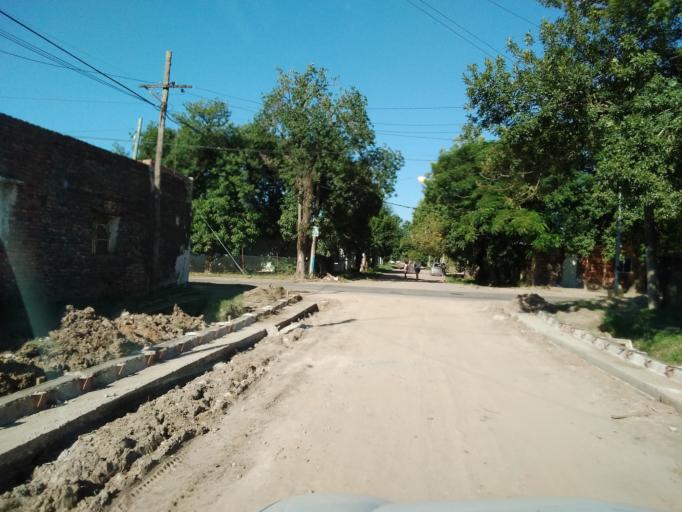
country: AR
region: Corrientes
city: Corrientes
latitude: -27.4843
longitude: -58.8072
